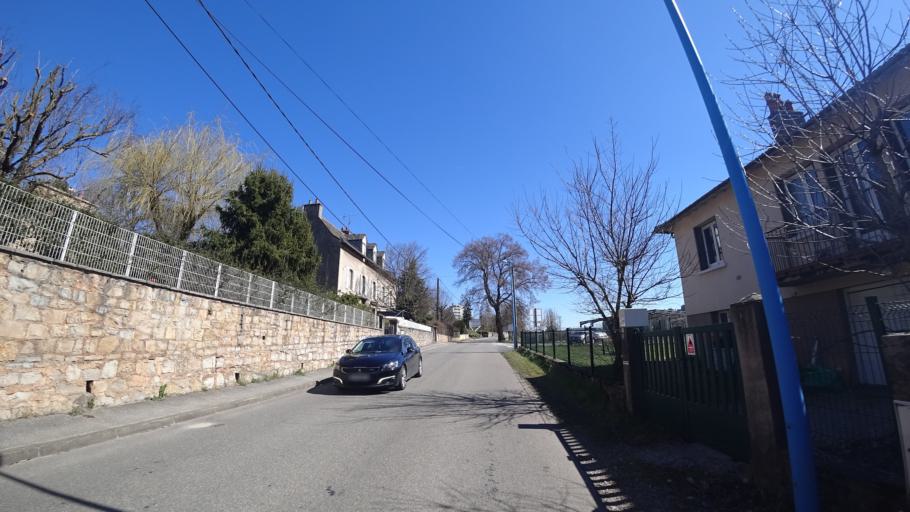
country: FR
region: Midi-Pyrenees
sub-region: Departement de l'Aveyron
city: Rodez
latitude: 44.3636
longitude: 2.5831
